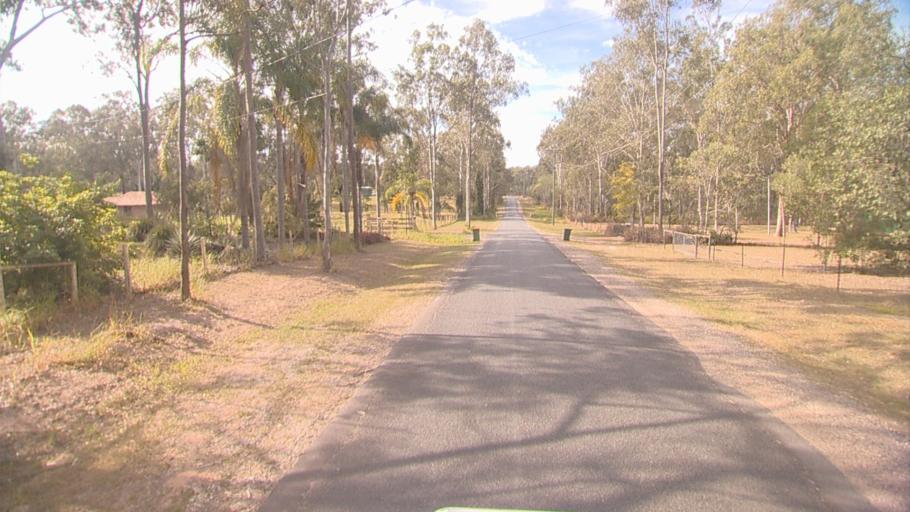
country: AU
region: Queensland
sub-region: Logan
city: North Maclean
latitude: -27.7481
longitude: 152.9831
